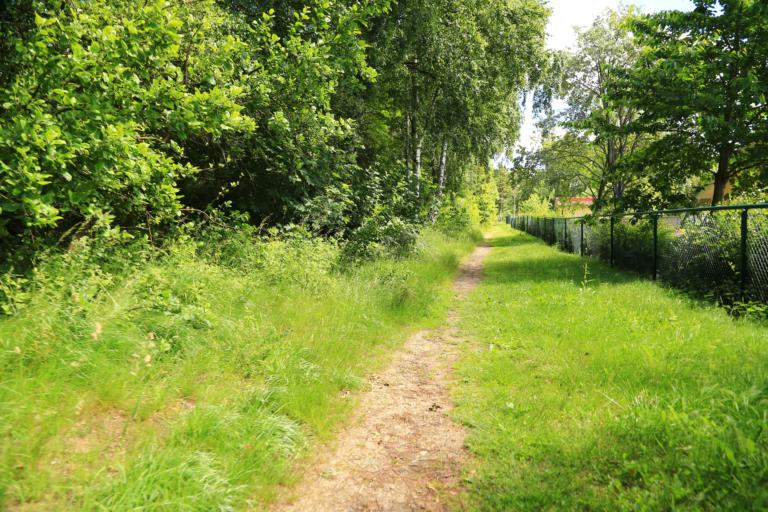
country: SE
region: Halland
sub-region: Varbergs Kommun
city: Varberg
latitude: 57.1157
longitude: 12.2787
